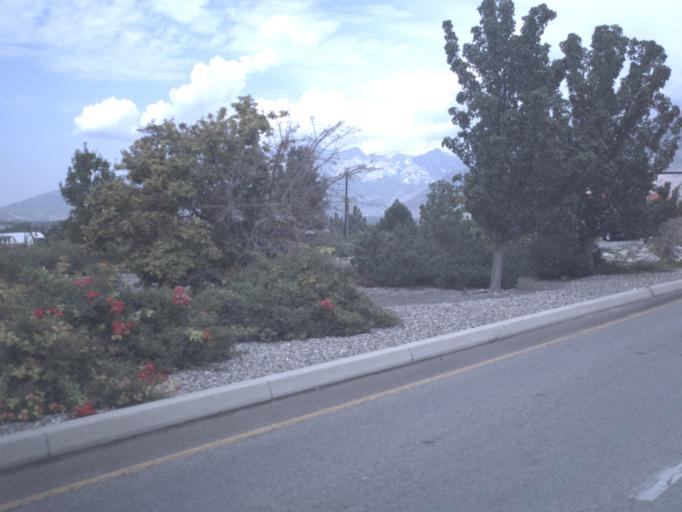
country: US
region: Utah
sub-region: Utah County
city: Pleasant Grove
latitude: 40.3486
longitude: -111.7698
